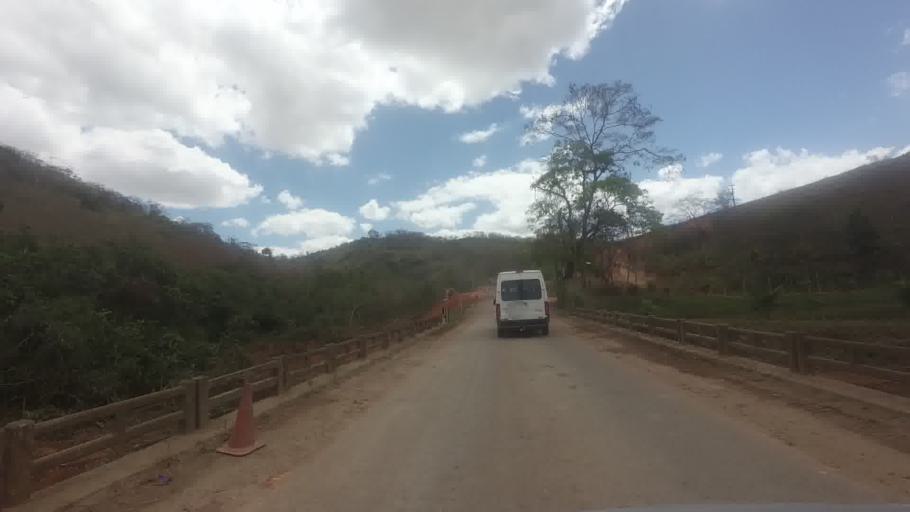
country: BR
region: Rio de Janeiro
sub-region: Santo Antonio De Padua
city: Santo Antonio de Padua
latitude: -21.5128
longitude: -42.0913
